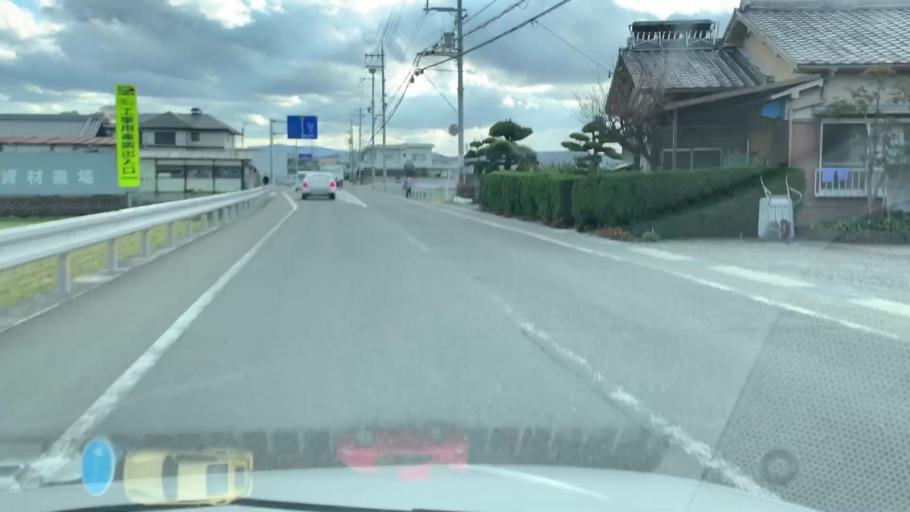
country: JP
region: Wakayama
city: Iwade
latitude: 34.2636
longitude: 135.2491
